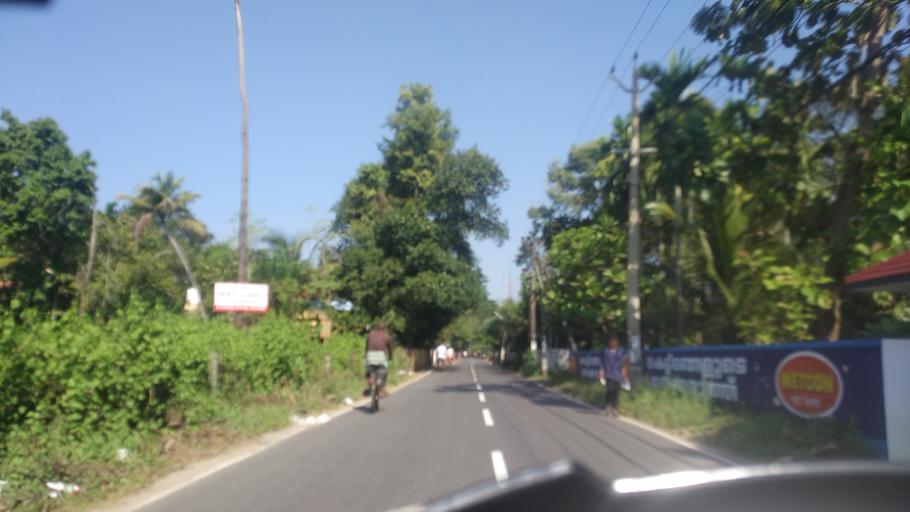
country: IN
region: Kerala
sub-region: Ernakulam
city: Elur
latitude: 10.1174
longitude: 76.2471
